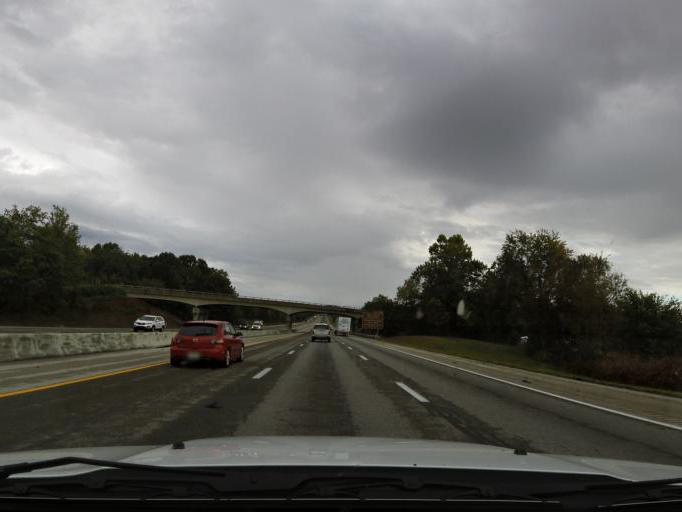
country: US
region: Kentucky
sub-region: Laurel County
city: London
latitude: 37.0872
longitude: -84.0997
